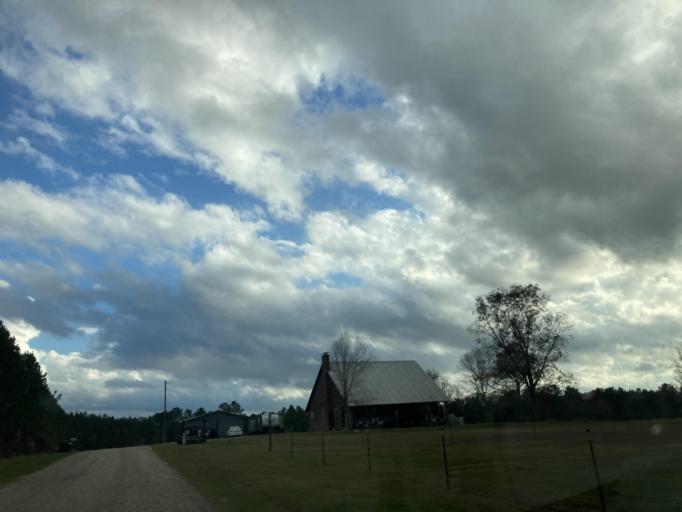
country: US
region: Mississippi
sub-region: Marion County
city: Columbia
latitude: 31.1782
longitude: -89.6646
